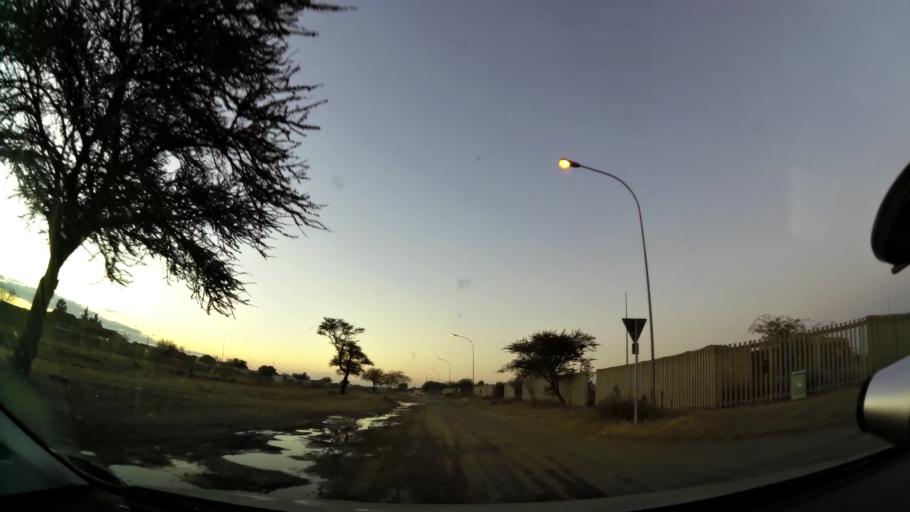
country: ZA
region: Northern Cape
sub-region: Frances Baard District Municipality
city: Kimberley
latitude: -28.7174
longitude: 24.7631
